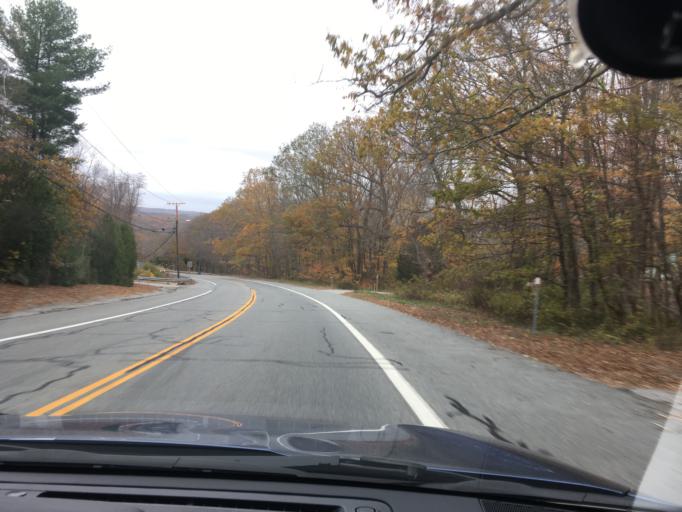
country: US
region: Rhode Island
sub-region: Providence County
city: Chepachet
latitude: 41.8429
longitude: -71.6789
